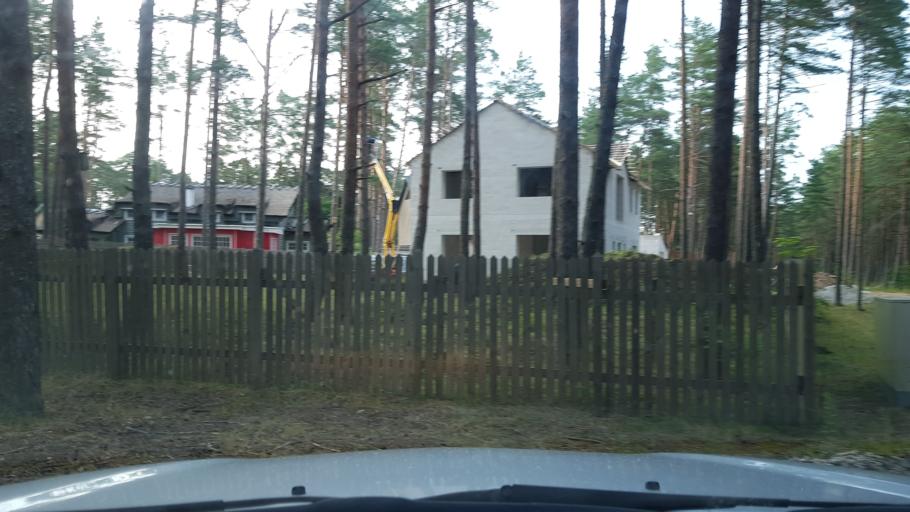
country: EE
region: Ida-Virumaa
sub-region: Narva-Joesuu linn
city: Narva-Joesuu
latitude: 59.4531
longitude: 28.0619
